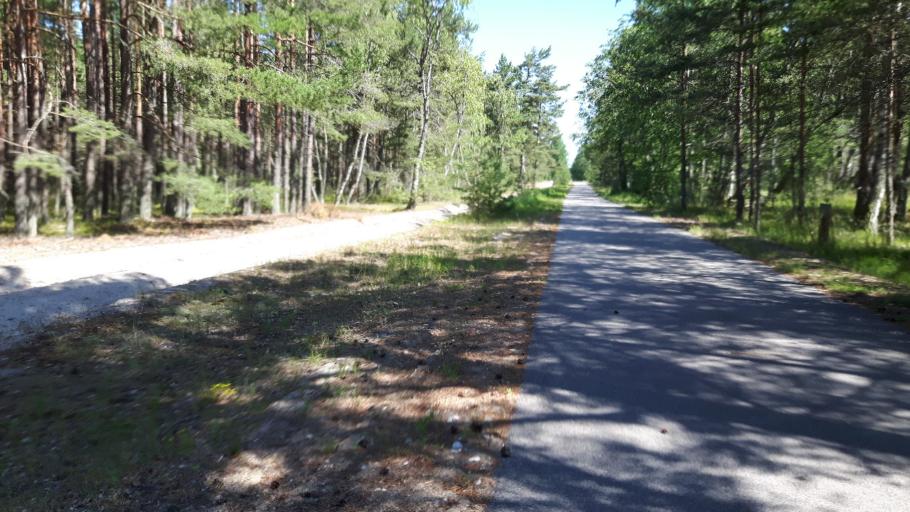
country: LT
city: Nida
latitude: 55.3367
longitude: 21.0363
